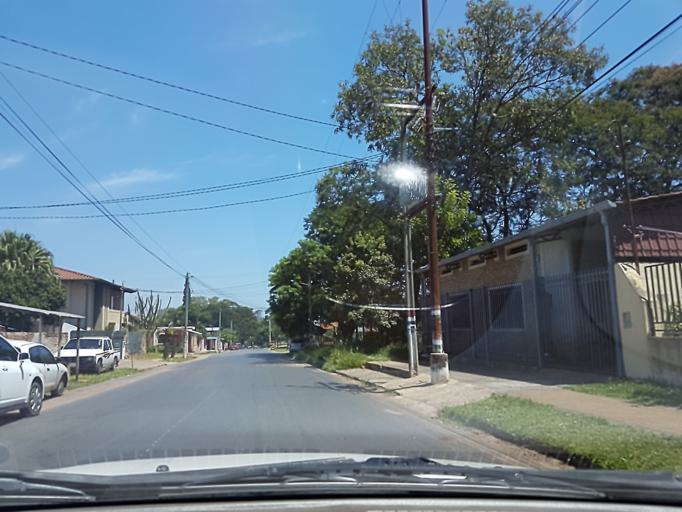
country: PY
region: Central
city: Fernando de la Mora
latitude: -25.2909
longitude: -57.5314
